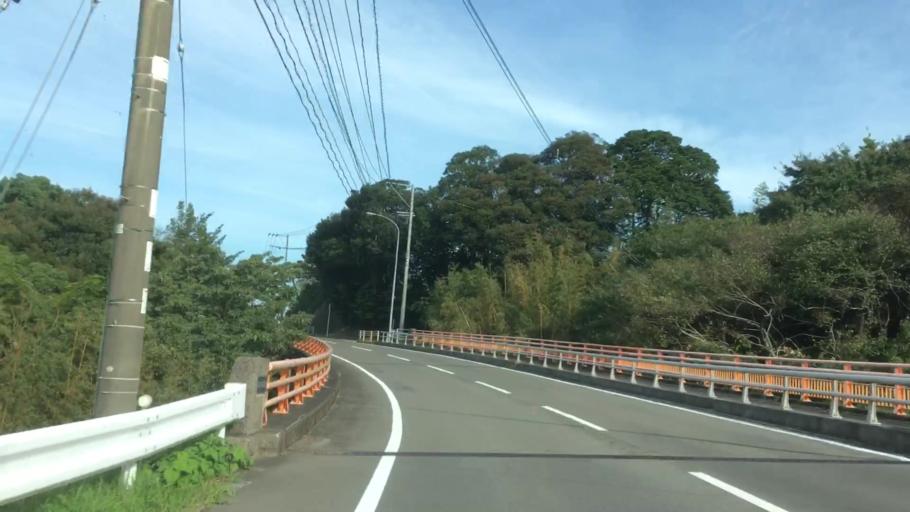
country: JP
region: Nagasaki
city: Sasebo
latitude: 33.0083
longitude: 129.6571
